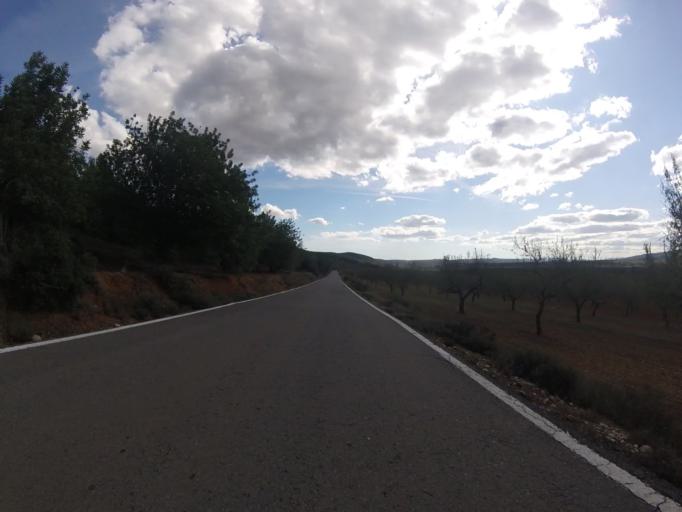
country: ES
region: Valencia
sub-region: Provincia de Castello
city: Cuevas de Vinroma
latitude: 40.3623
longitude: 0.1238
